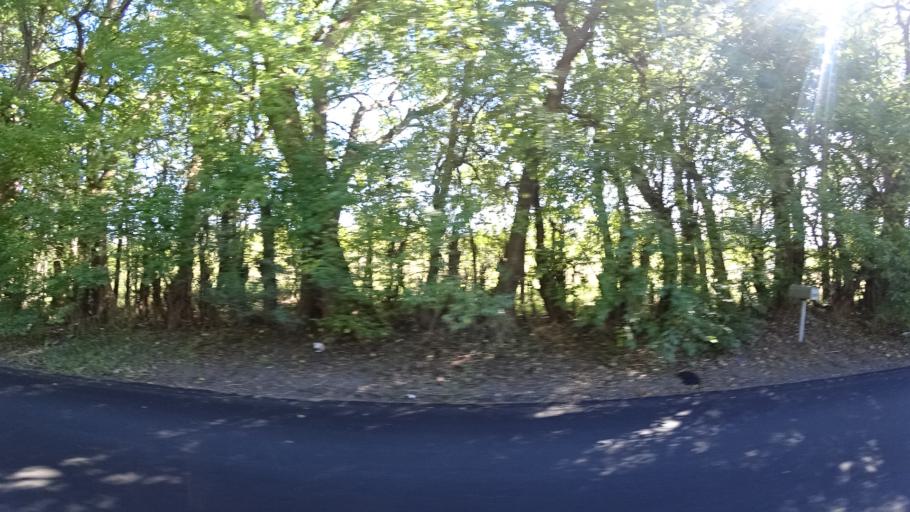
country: US
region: Indiana
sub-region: LaPorte County
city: Michigan City
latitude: 41.6908
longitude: -86.9131
